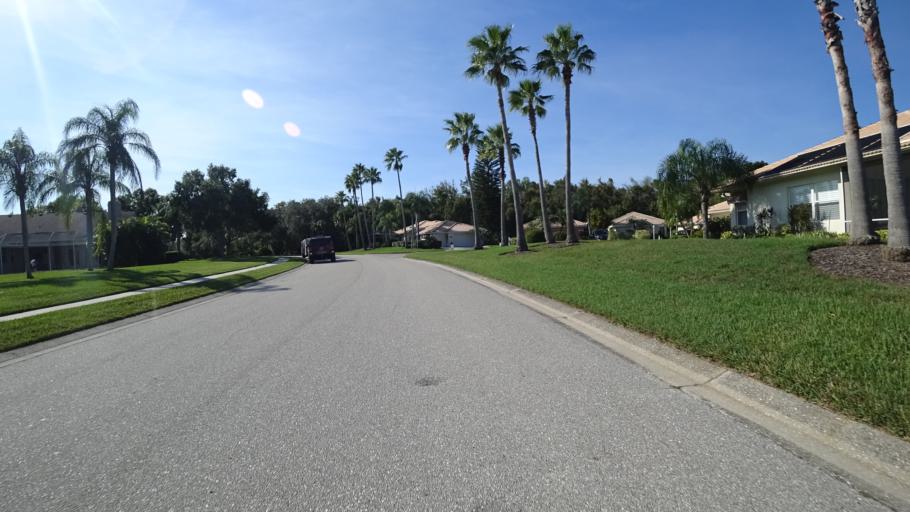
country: US
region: Florida
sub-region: Sarasota County
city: The Meadows
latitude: 27.4224
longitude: -82.4366
